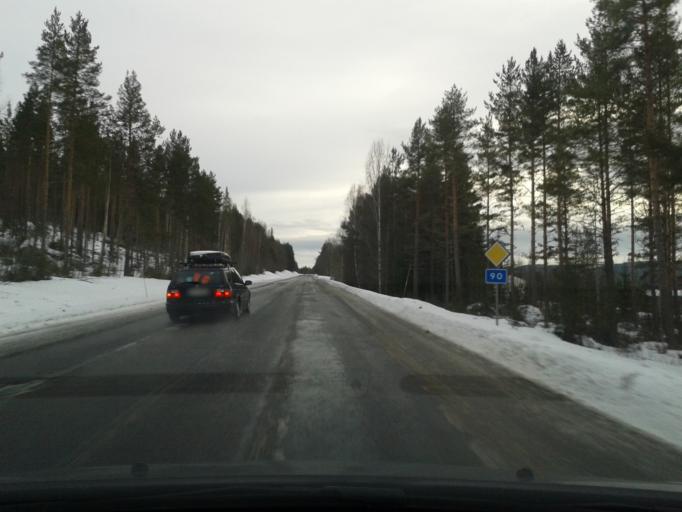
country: SE
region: Vaesternorrland
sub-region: Solleftea Kommun
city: As
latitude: 63.5444
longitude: 16.8427
